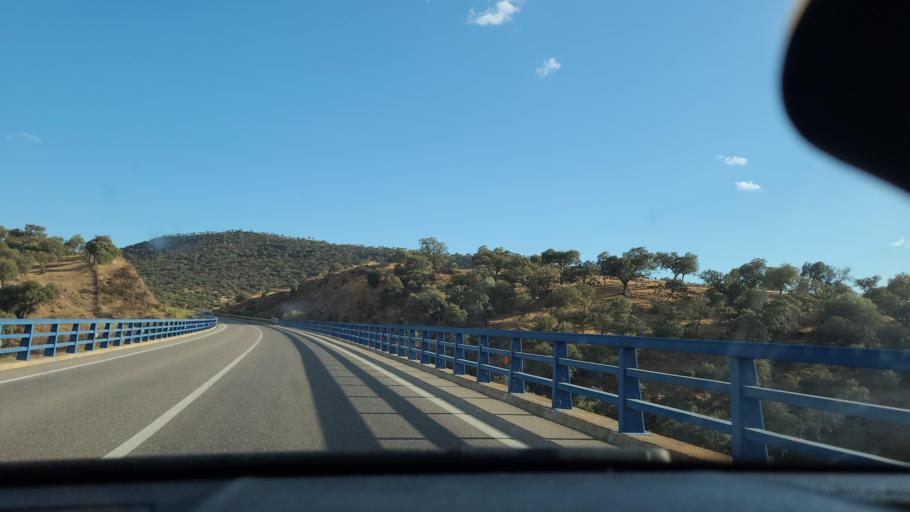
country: ES
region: Andalusia
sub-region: Province of Cordoba
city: Belmez
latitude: 38.2340
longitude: -5.1679
